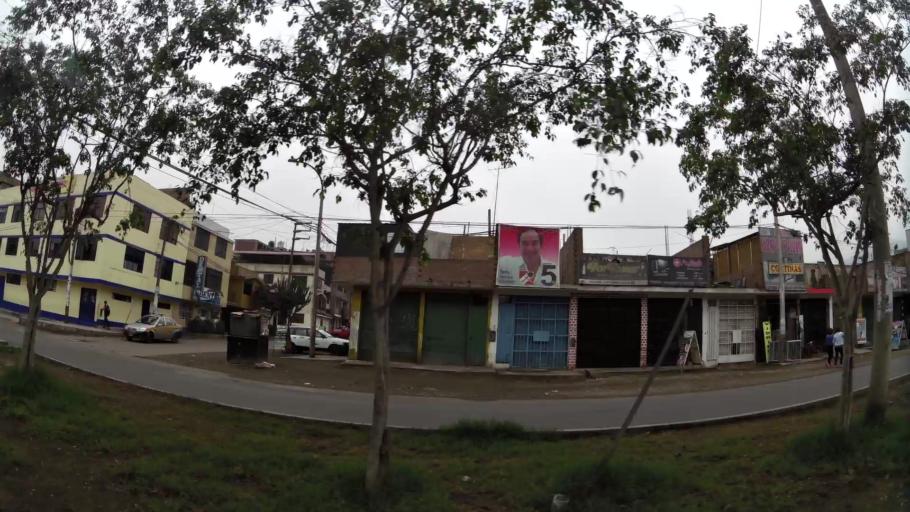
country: PE
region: Lima
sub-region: Lima
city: Independencia
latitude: -11.9493
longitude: -76.9826
